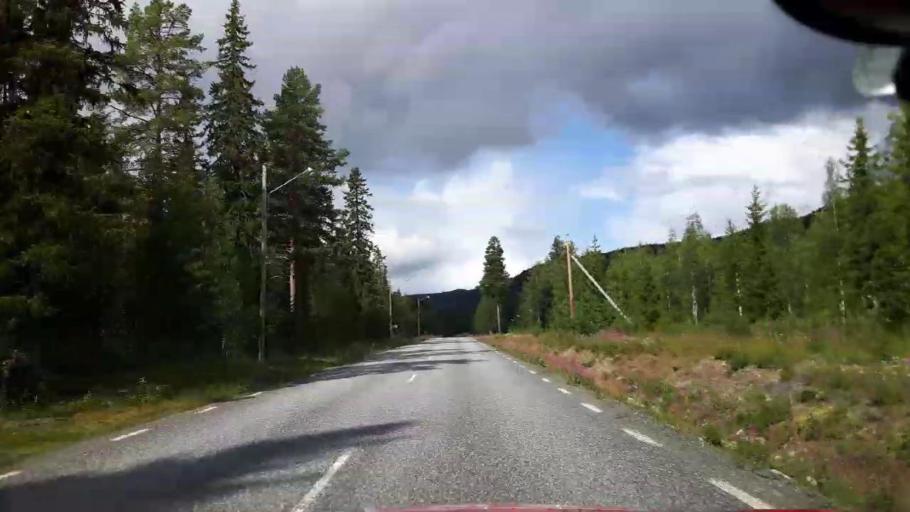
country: SE
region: Vaesterbotten
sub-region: Vilhelmina Kommun
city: Sjoberg
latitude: 64.9408
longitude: 15.8455
